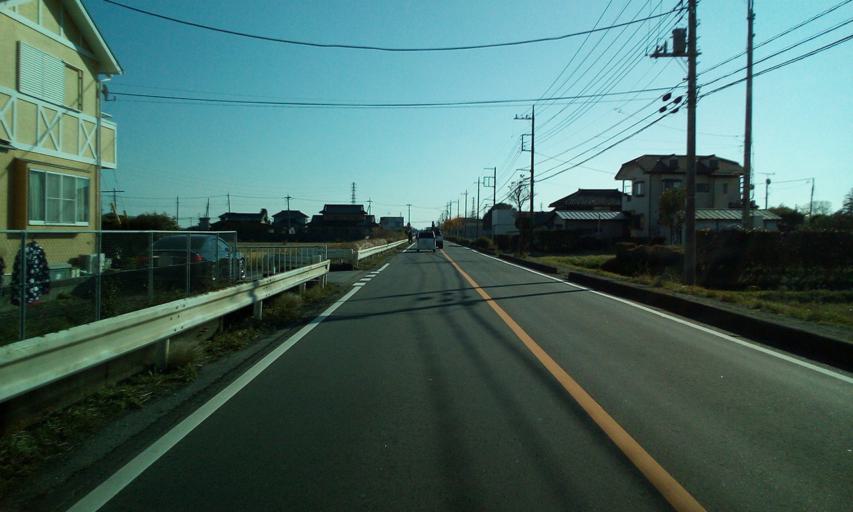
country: JP
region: Saitama
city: Kasukabe
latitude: 36.0220
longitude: 139.7900
